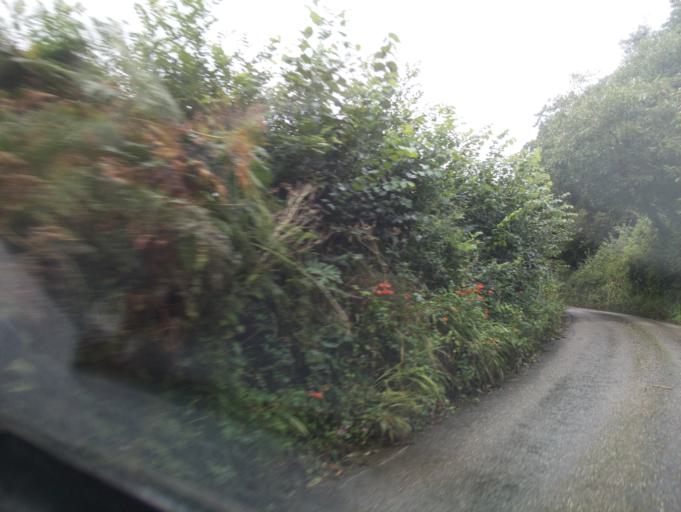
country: GB
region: England
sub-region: Devon
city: Totnes
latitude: 50.3503
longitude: -3.6707
